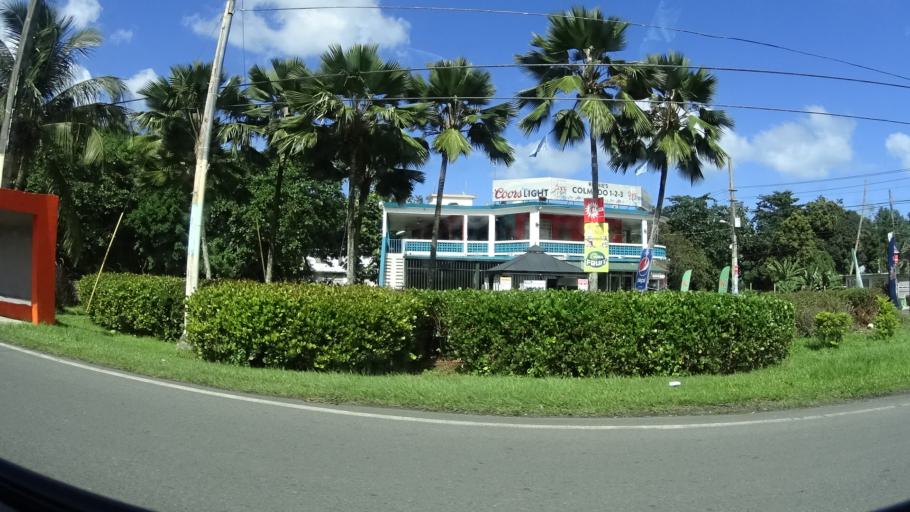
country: PR
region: Rio Grande
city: Palmer
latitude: 18.3721
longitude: -65.7678
